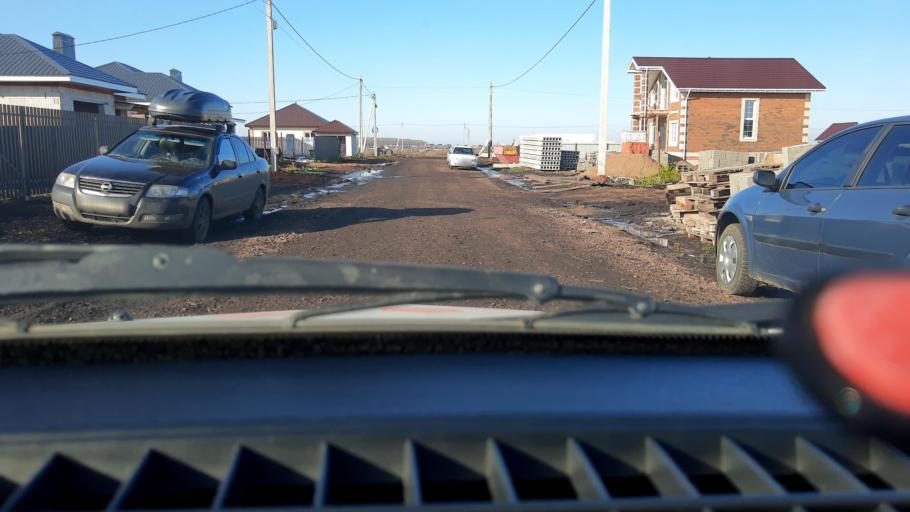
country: RU
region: Bashkortostan
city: Kabakovo
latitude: 54.6281
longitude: 56.1385
